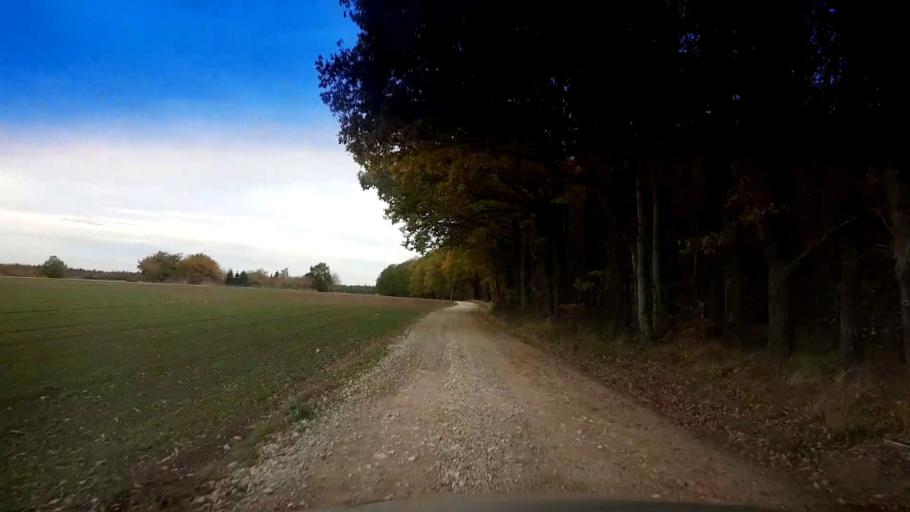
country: DE
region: Bavaria
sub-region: Upper Franconia
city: Priesendorf
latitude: 49.9136
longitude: 10.7292
